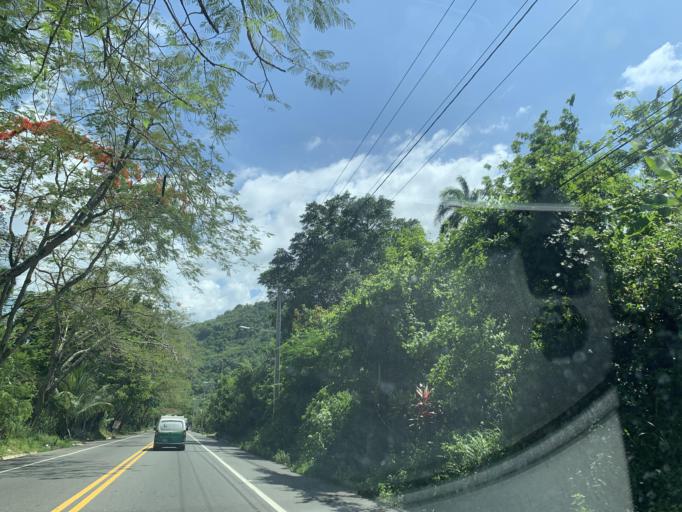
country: DO
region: Puerto Plata
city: Altamira
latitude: 19.6997
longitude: -70.8400
